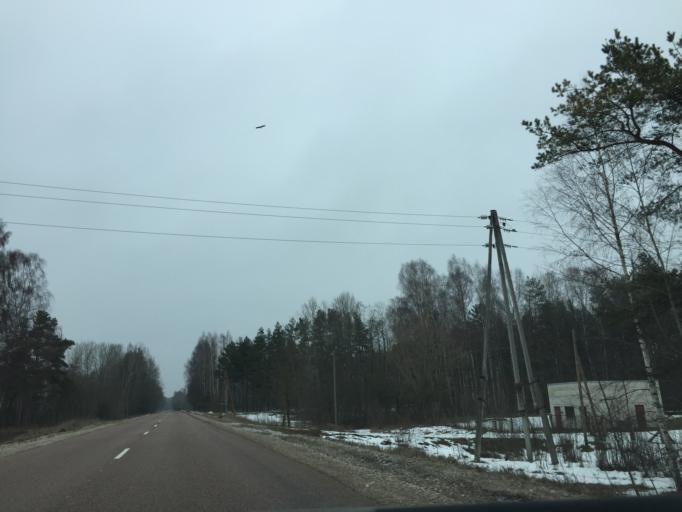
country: LV
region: Olaine
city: Olaine
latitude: 56.6305
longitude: 23.9335
